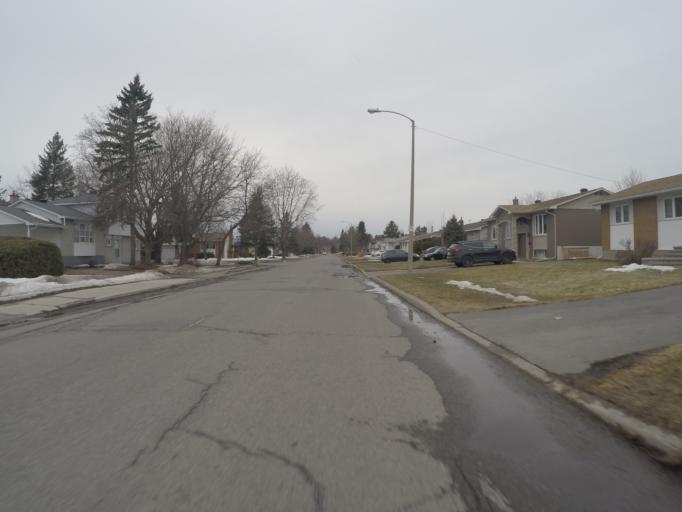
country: CA
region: Quebec
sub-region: Outaouais
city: Gatineau
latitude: 45.4695
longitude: -75.5030
